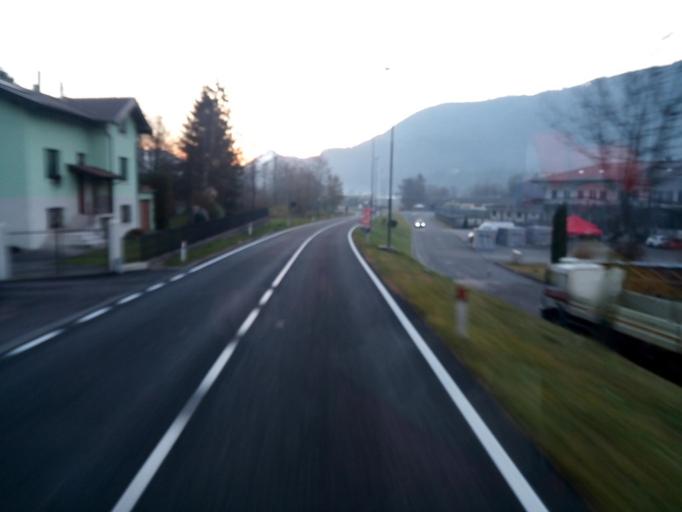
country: IT
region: Friuli Venezia Giulia
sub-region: Provincia di Udine
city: Villa Santina
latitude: 46.4147
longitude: 12.9313
